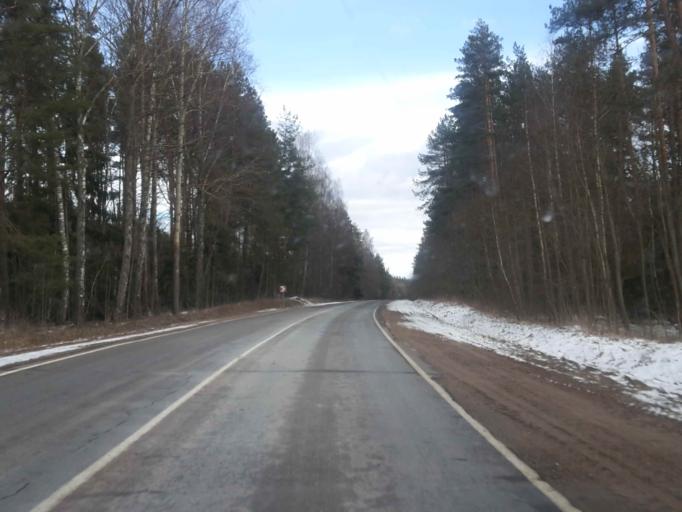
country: BY
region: Minsk
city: Myadzyel
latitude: 54.7780
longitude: 27.0531
